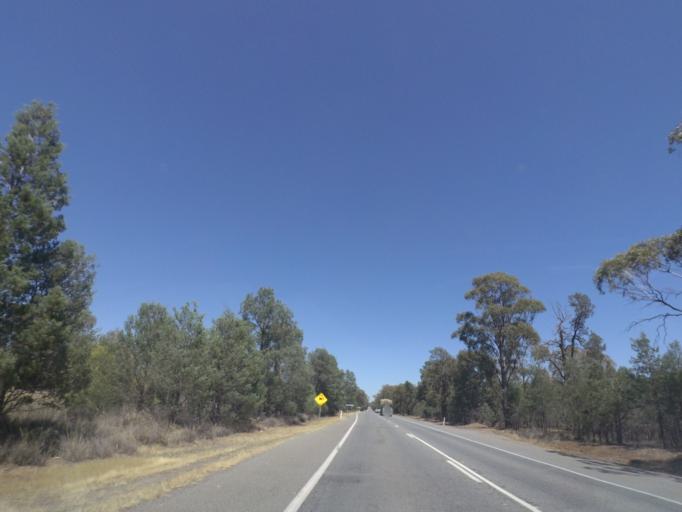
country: AU
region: New South Wales
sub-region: Narrandera
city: Narrandera
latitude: -34.7363
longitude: 146.5977
